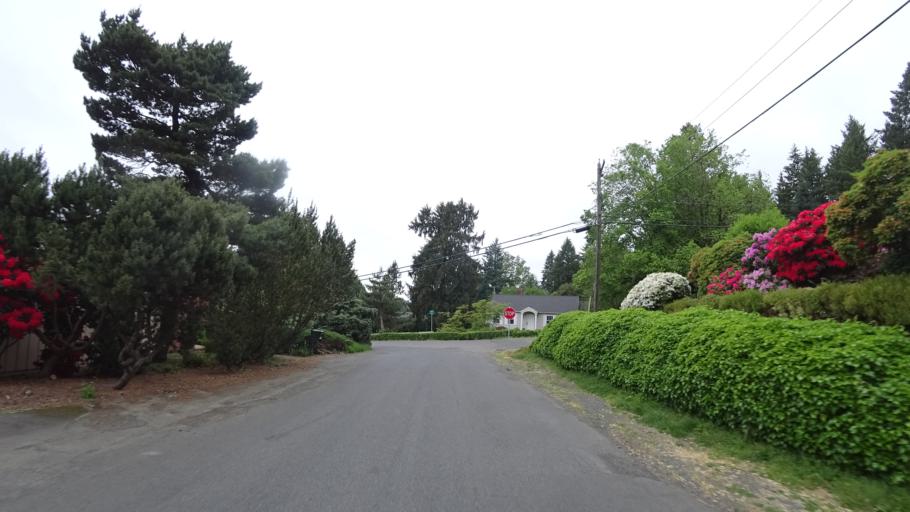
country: US
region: Oregon
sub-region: Multnomah County
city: Portland
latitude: 45.4820
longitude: -122.6957
